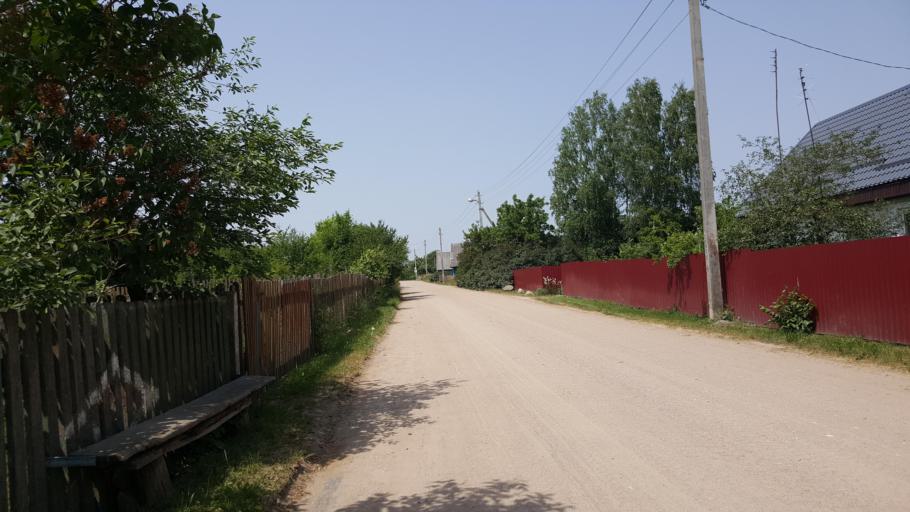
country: BY
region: Brest
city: Kamyanyets
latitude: 52.4799
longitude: 23.8789
